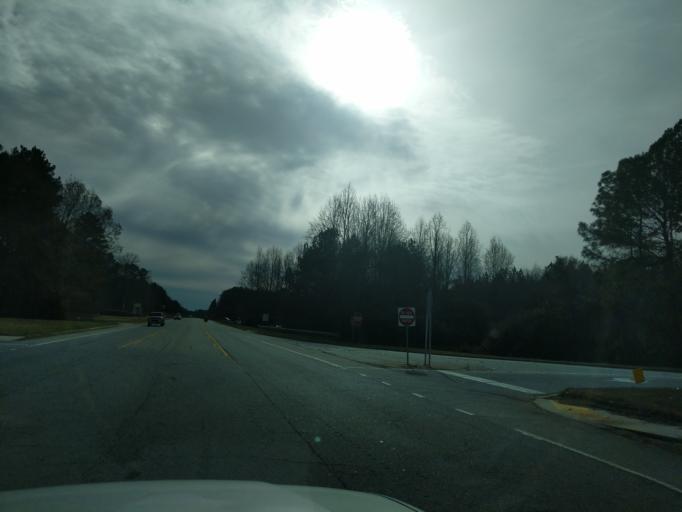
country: US
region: South Carolina
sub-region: Oconee County
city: Walhalla
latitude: 34.7567
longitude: -83.0460
